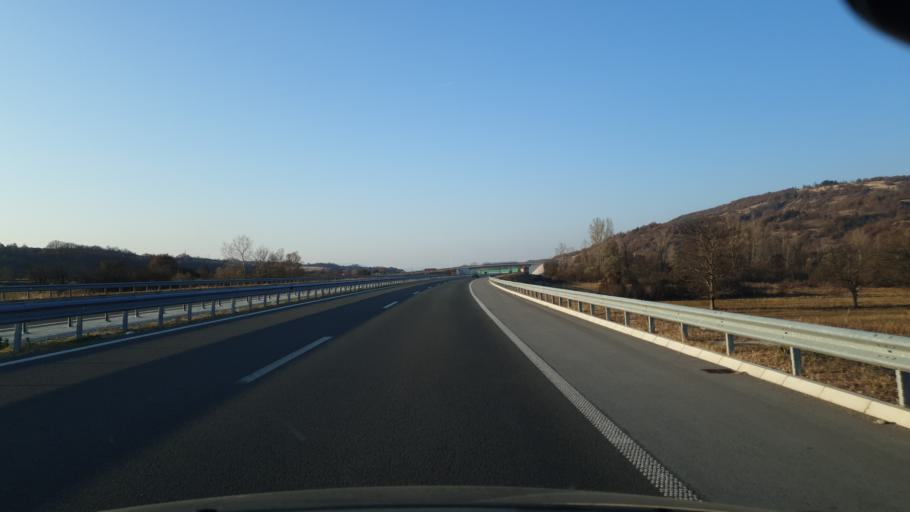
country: RS
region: Central Serbia
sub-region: Pirotski Okrug
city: Dimitrovgrad
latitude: 43.0408
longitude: 22.7102
